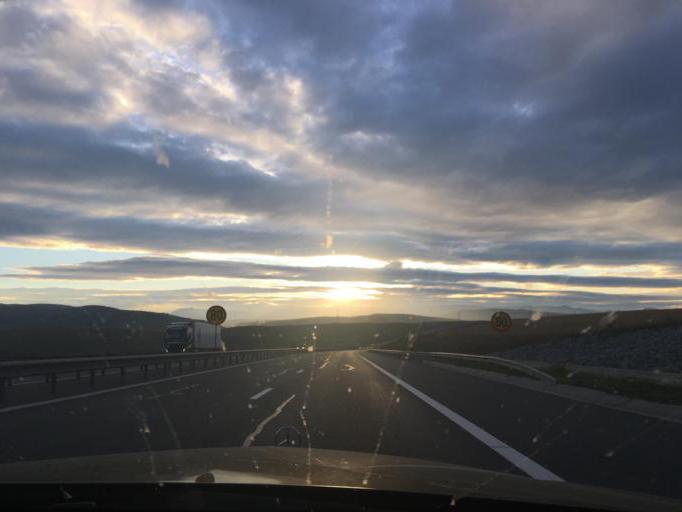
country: RO
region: Cluj
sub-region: Comuna Petrestii De Jos
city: Petrestii de Jos
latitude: 46.5986
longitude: 23.6589
